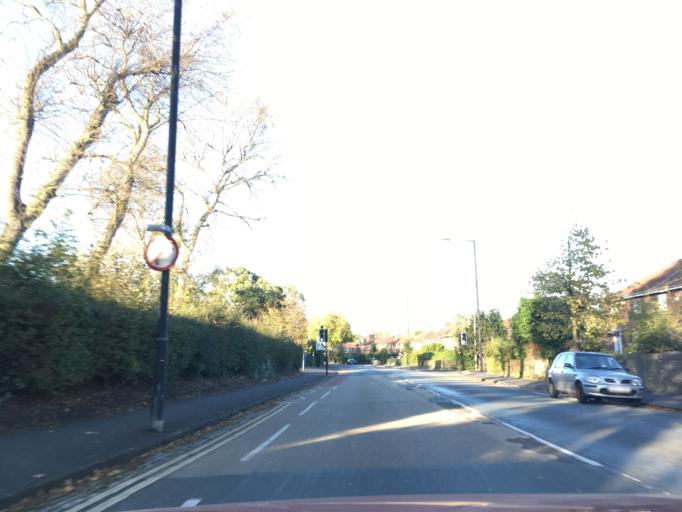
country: GB
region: England
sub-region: South Gloucestershire
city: Stoke Gifford
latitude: 51.4981
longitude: -2.5800
